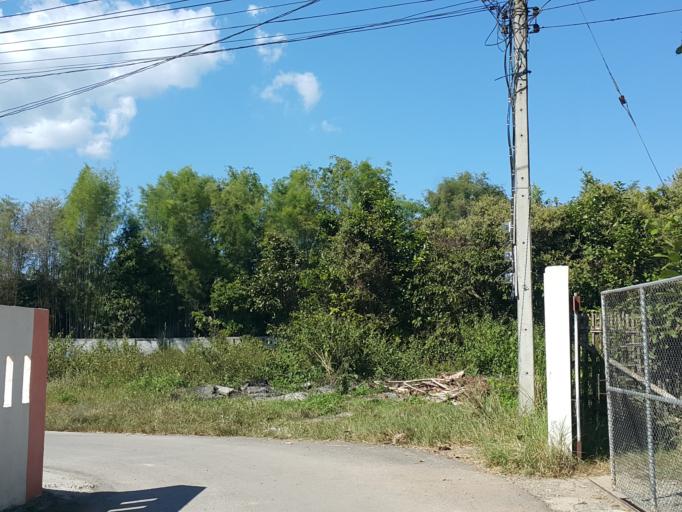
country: TH
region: Chiang Mai
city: San Sai
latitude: 18.8830
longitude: 99.1462
